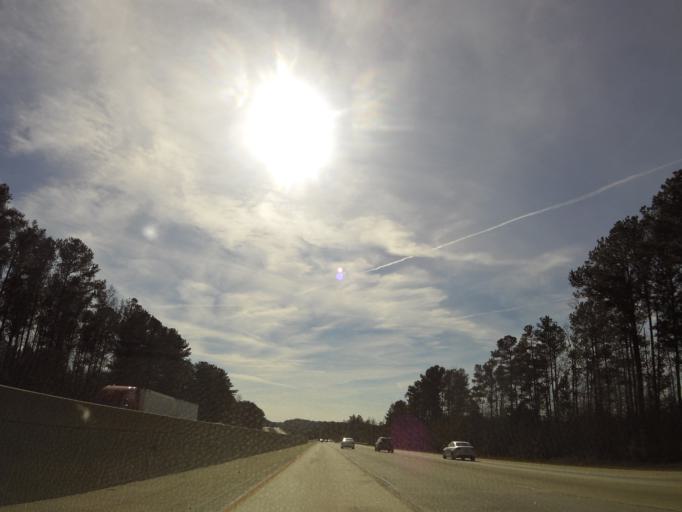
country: US
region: Georgia
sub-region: Fulton County
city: Palmetto
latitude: 33.4690
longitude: -84.6682
